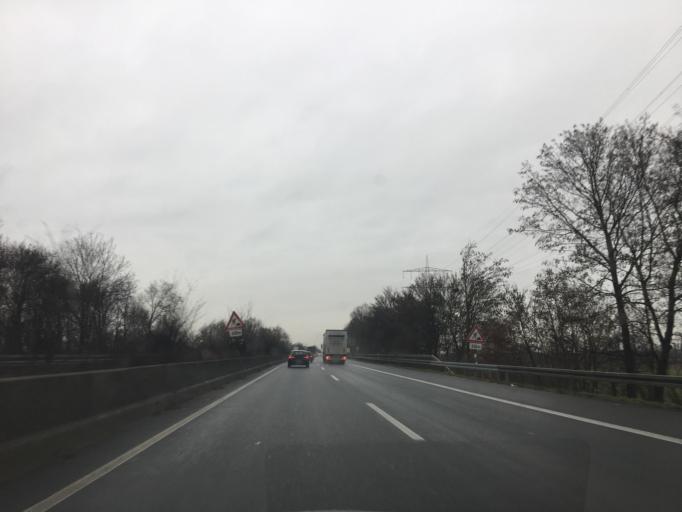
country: DE
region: North Rhine-Westphalia
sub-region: Regierungsbezirk Dusseldorf
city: Dormagen
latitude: 51.1047
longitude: 6.8003
